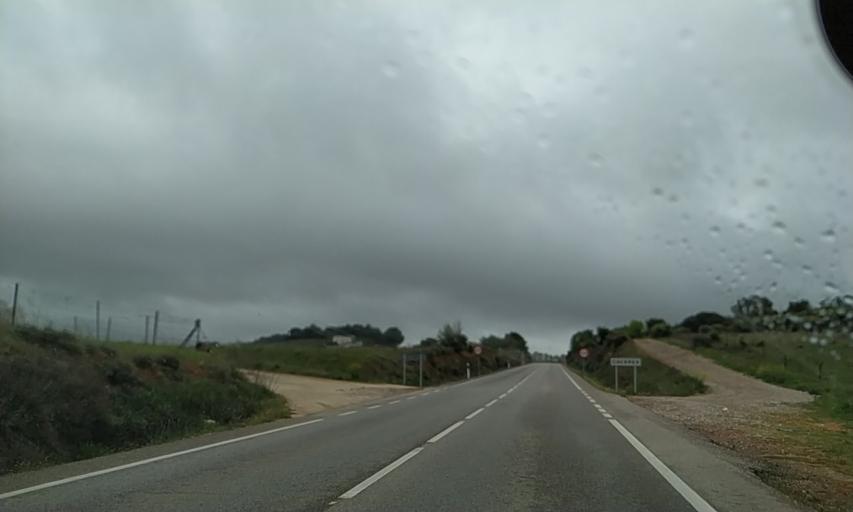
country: ES
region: Extremadura
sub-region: Provincia de Caceres
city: Caceres
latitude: 39.4906
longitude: -6.3841
